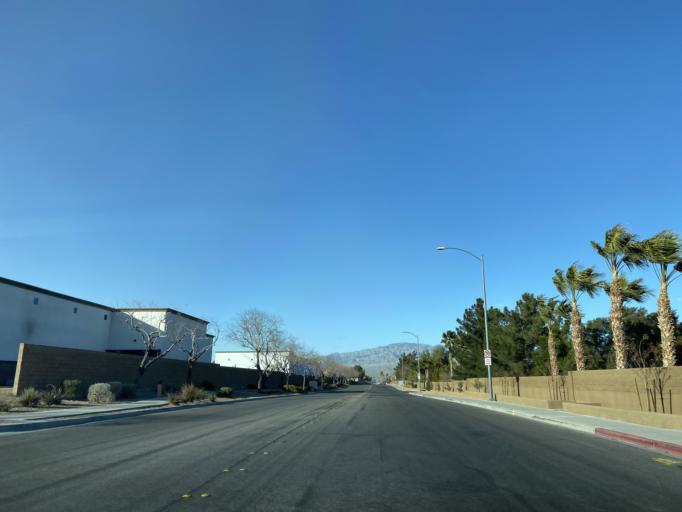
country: US
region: Nevada
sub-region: Clark County
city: Las Vegas
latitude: 36.2999
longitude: -115.2786
